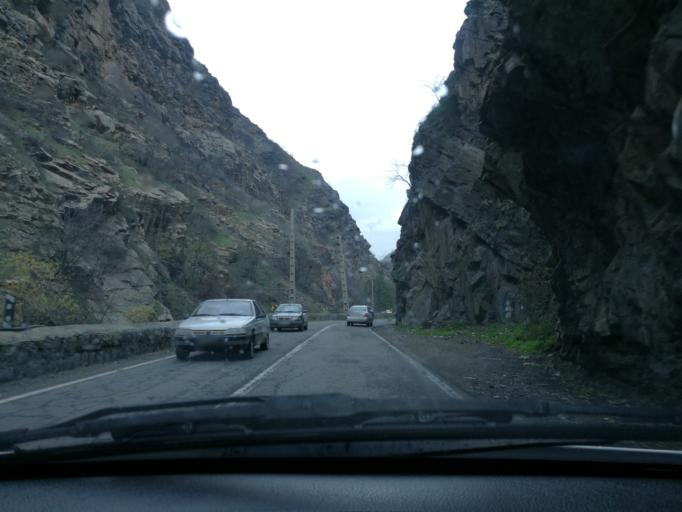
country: IR
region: Mazandaran
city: Chalus
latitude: 36.2955
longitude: 51.2459
